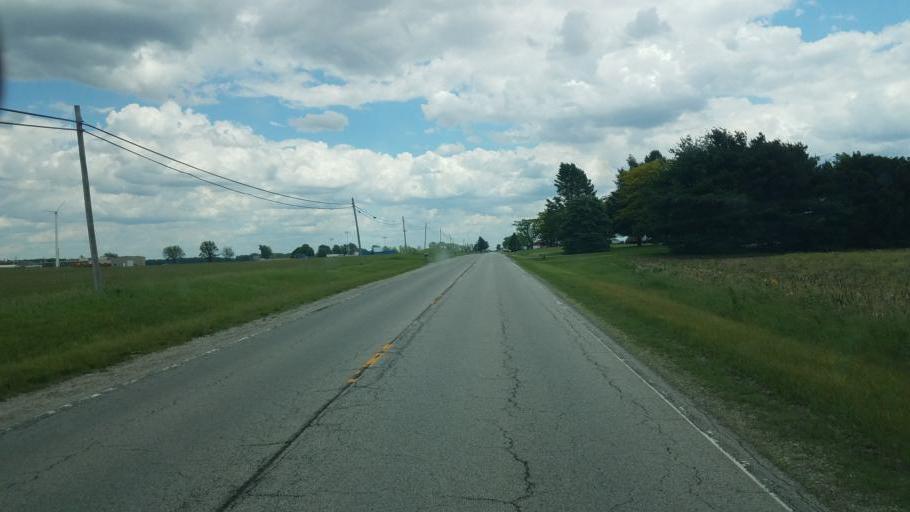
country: US
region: Ohio
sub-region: Crawford County
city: Bucyrus
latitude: 40.8219
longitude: -83.0259
